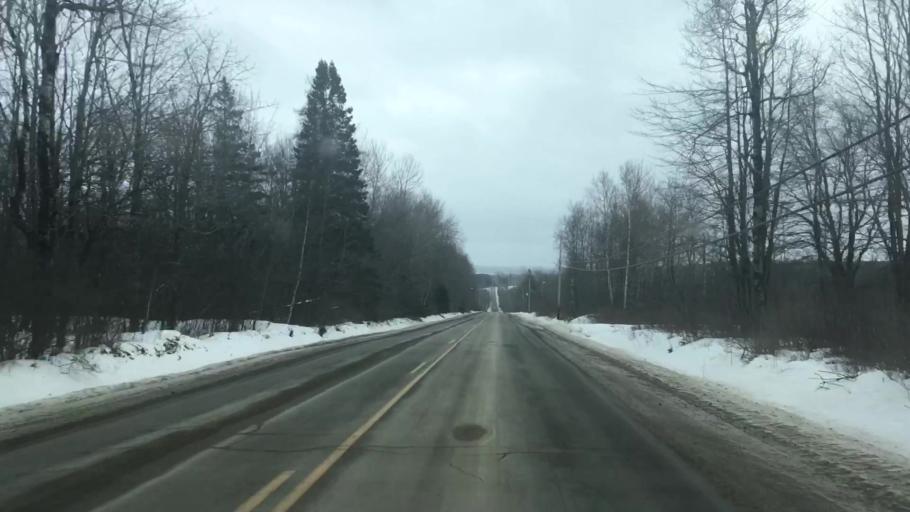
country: US
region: Maine
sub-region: Washington County
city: East Machias
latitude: 44.9745
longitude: -67.4501
